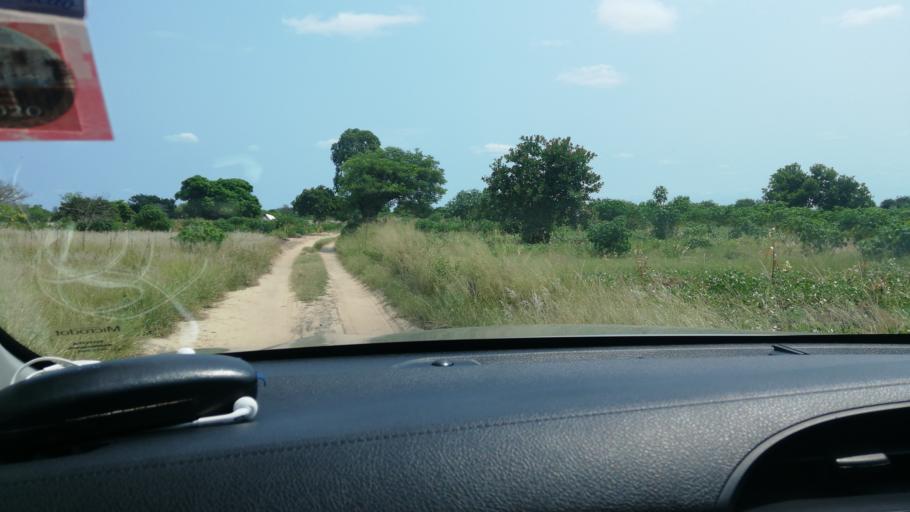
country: MZ
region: Maputo
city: Matola
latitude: -26.1102
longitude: 32.4205
